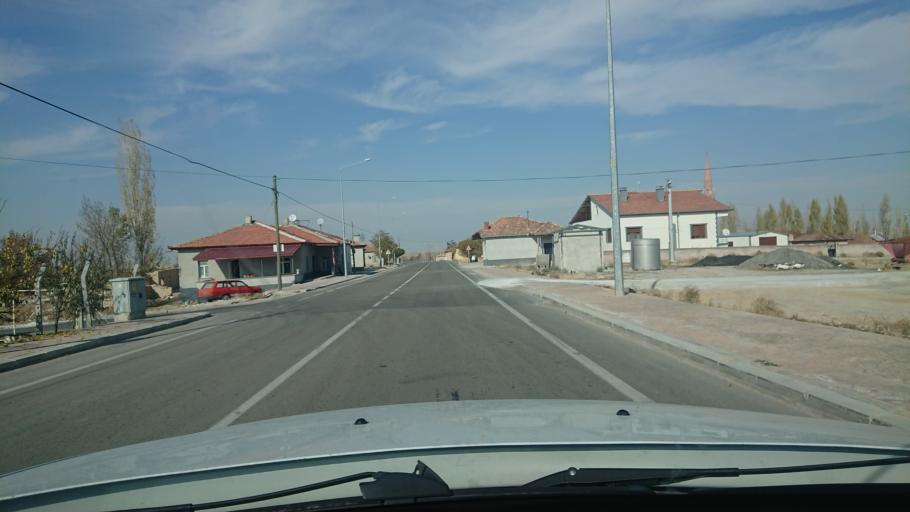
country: TR
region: Aksaray
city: Sultanhani
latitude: 38.2668
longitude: 33.4403
